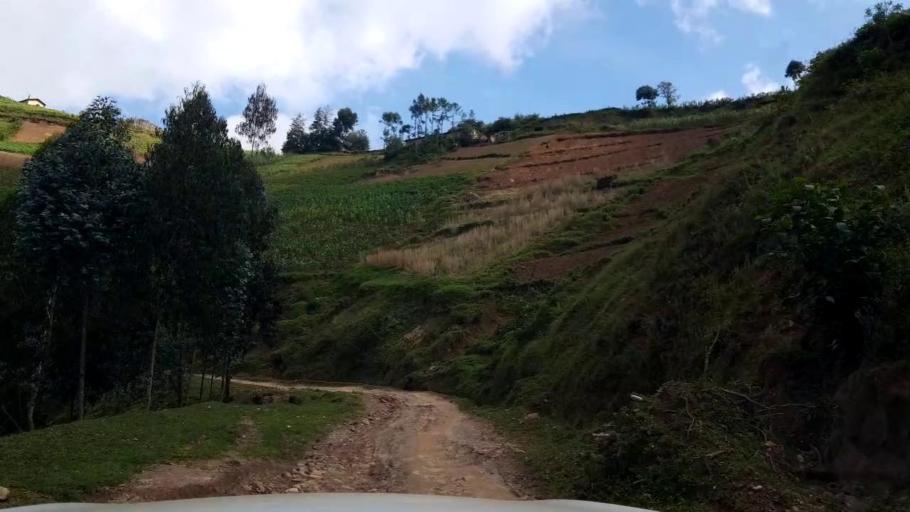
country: RW
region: Western Province
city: Kibuye
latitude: -1.8819
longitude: 29.4708
